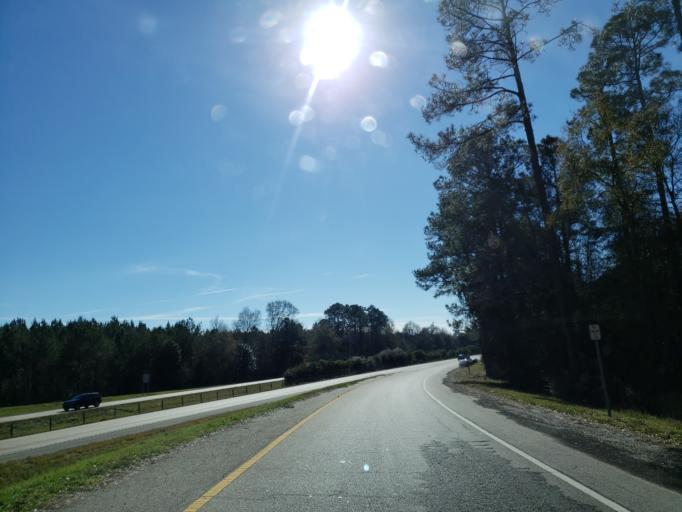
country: US
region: Mississippi
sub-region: Forrest County
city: Glendale
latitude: 31.3813
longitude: -89.3246
